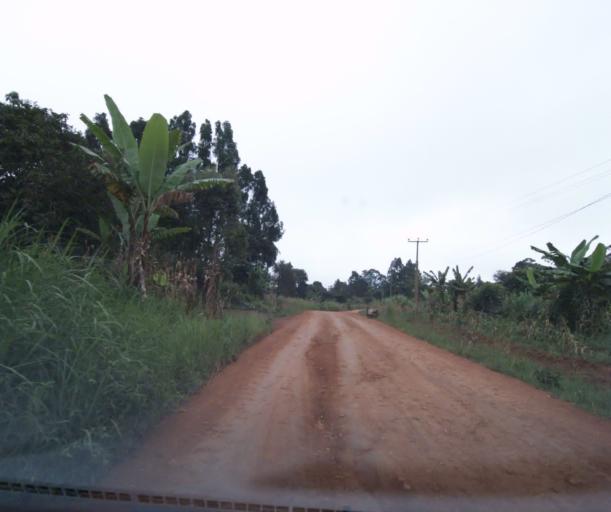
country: CM
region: West
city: Dschang
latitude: 5.5044
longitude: 10.0070
